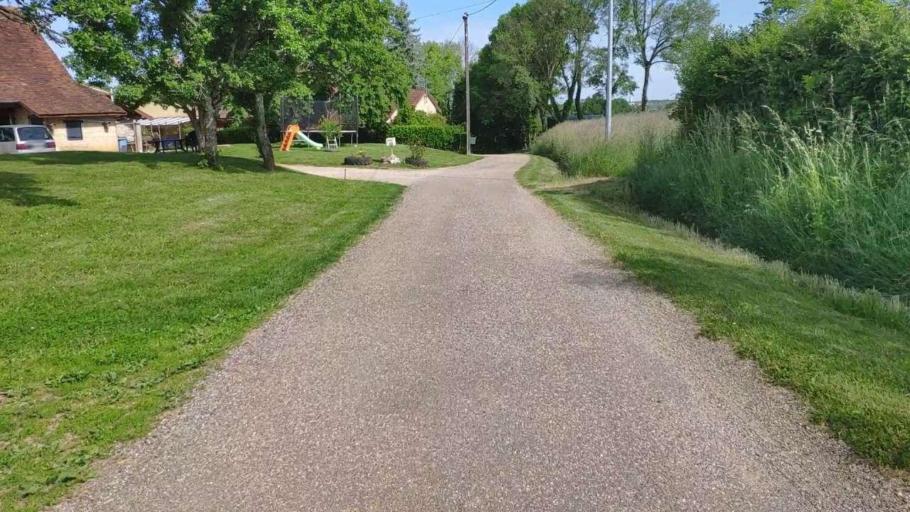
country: FR
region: Franche-Comte
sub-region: Departement du Jura
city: Bletterans
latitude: 46.7155
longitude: 5.4565
